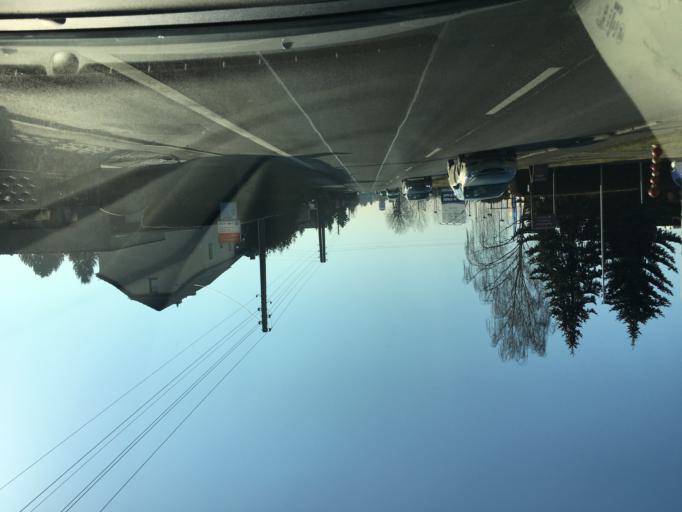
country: DE
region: Saxony
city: Grossposna
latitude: 51.2664
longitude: 12.4940
